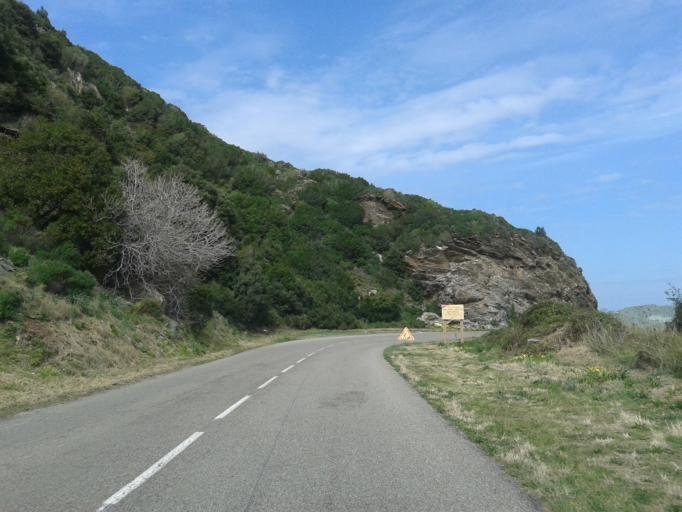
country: FR
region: Corsica
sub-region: Departement de la Haute-Corse
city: Brando
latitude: 42.8632
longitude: 9.4813
